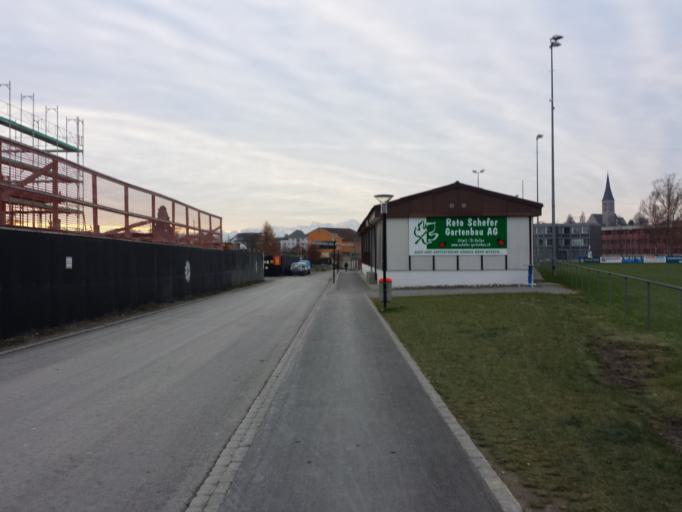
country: CH
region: Thurgau
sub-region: Arbon District
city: Romanshorn
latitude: 47.5701
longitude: 9.3731
